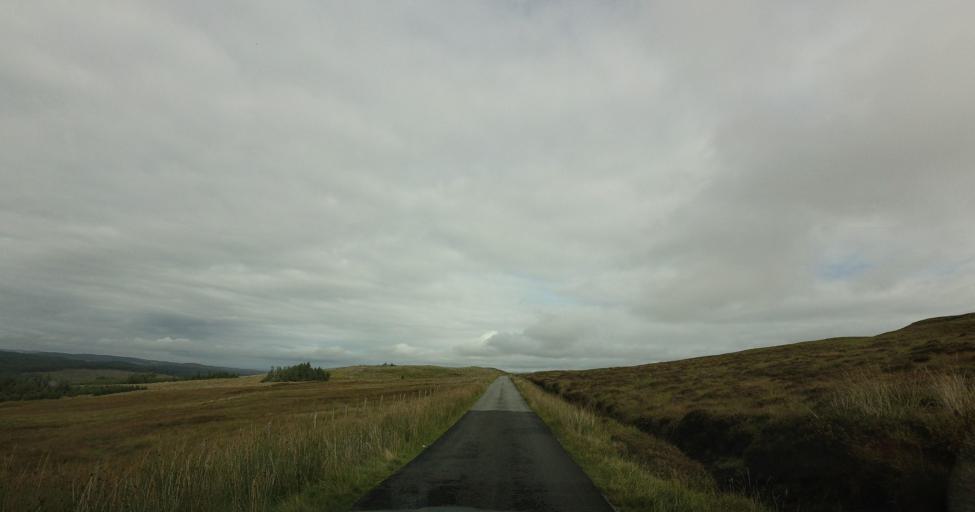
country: GB
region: Scotland
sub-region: Highland
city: Isle of Skye
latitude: 57.3967
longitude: -6.2707
